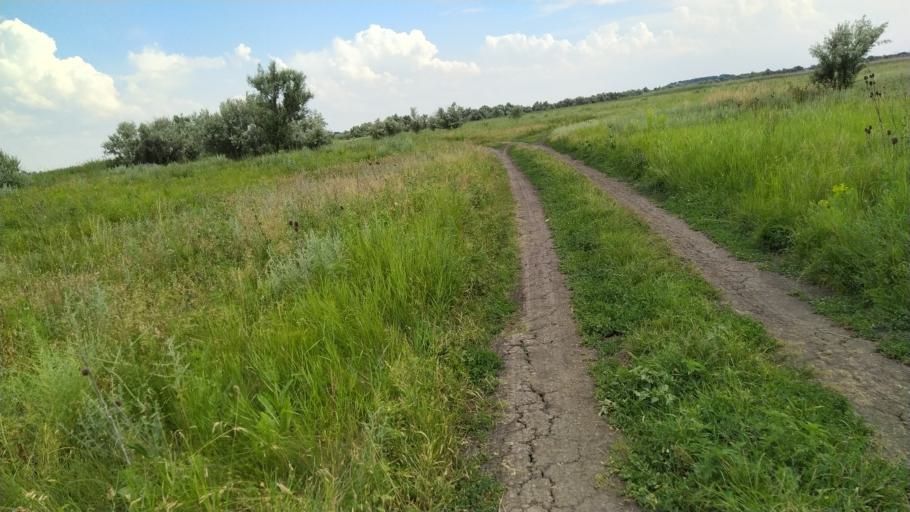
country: RU
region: Rostov
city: Kuleshovka
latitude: 47.1302
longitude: 39.6294
